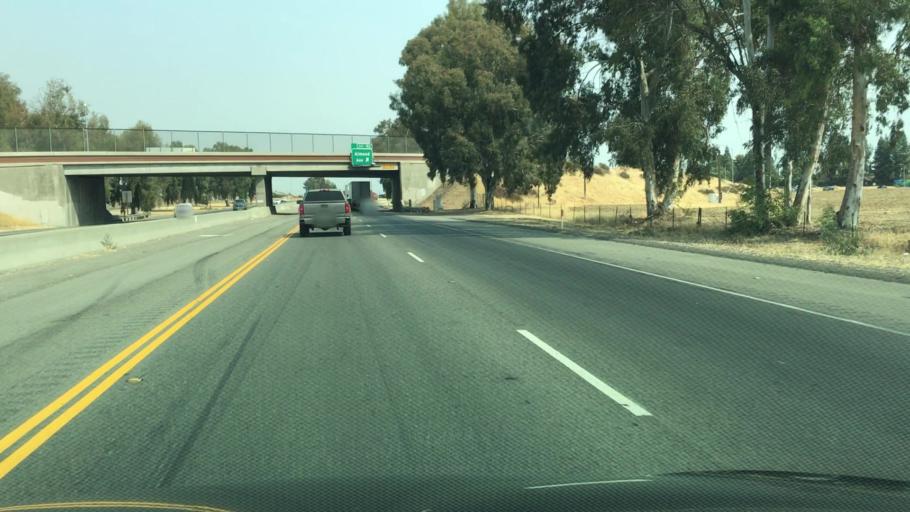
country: US
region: California
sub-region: Madera County
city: Madera
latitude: 36.9494
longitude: -120.0494
